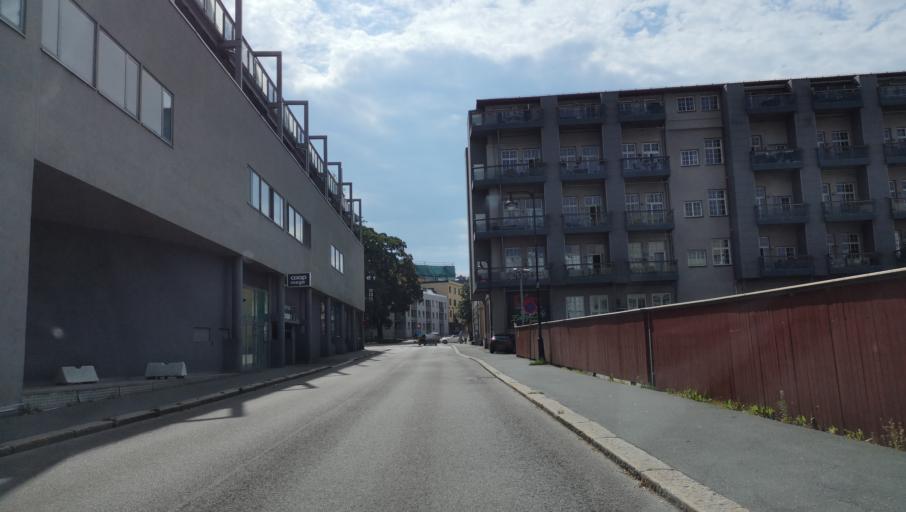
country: NO
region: Ostfold
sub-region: Moss
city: Moss
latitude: 59.4371
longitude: 10.6616
